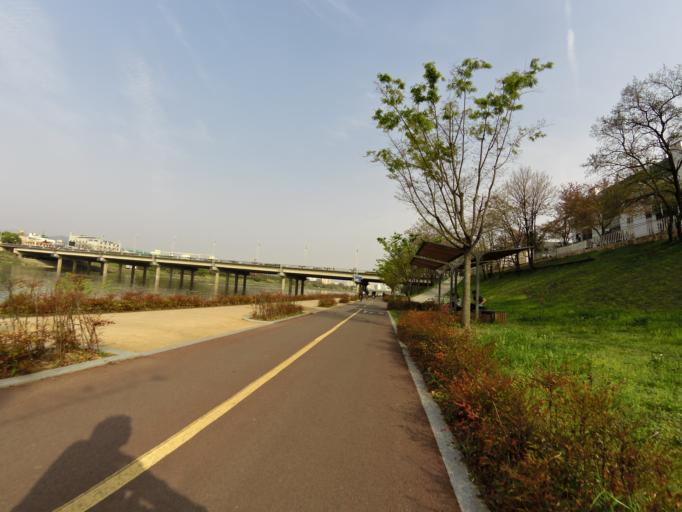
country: KR
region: Daegu
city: Daegu
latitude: 35.8886
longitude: 128.6396
